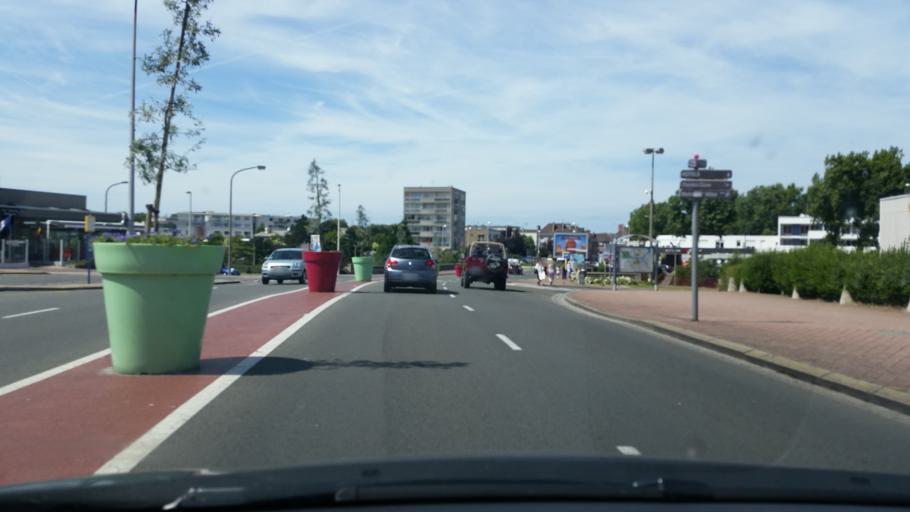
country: FR
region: Nord-Pas-de-Calais
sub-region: Departement du Pas-de-Calais
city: Calais
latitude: 50.9535
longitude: 1.8515
